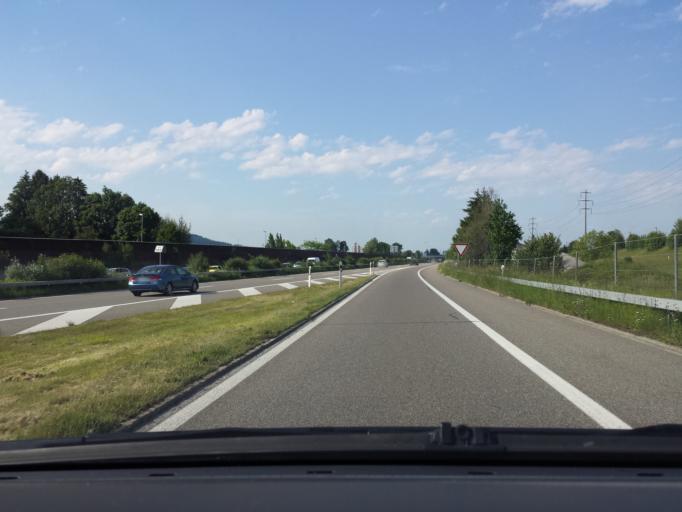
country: CH
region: Saint Gallen
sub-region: Wahlkreis Rheintal
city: Diepoldsau
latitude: 47.3933
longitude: 9.6450
